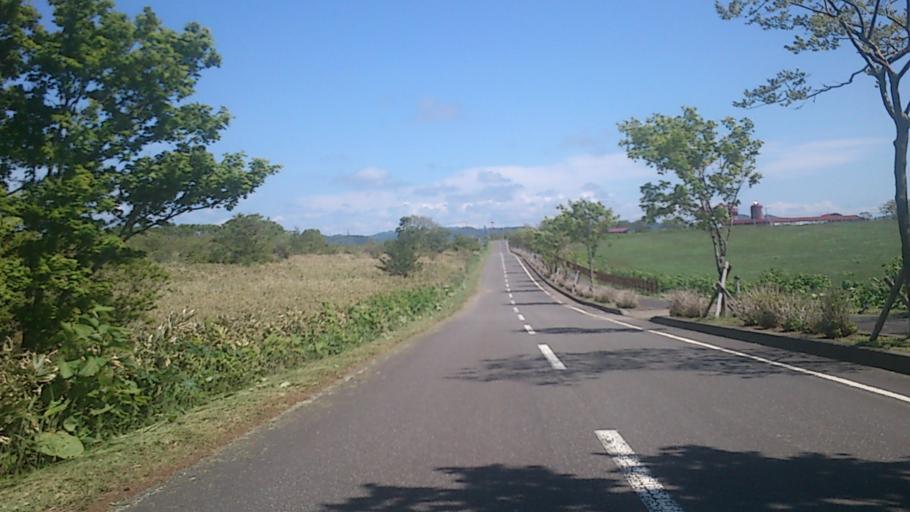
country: JP
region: Hokkaido
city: Rumoi
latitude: 44.5602
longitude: 141.7786
